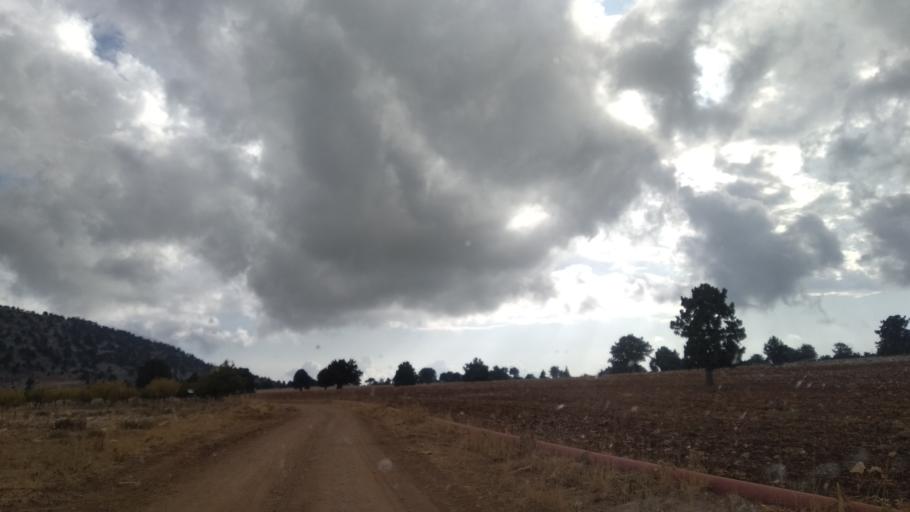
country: TR
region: Mersin
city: Sarikavak
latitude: 36.5647
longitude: 33.7381
